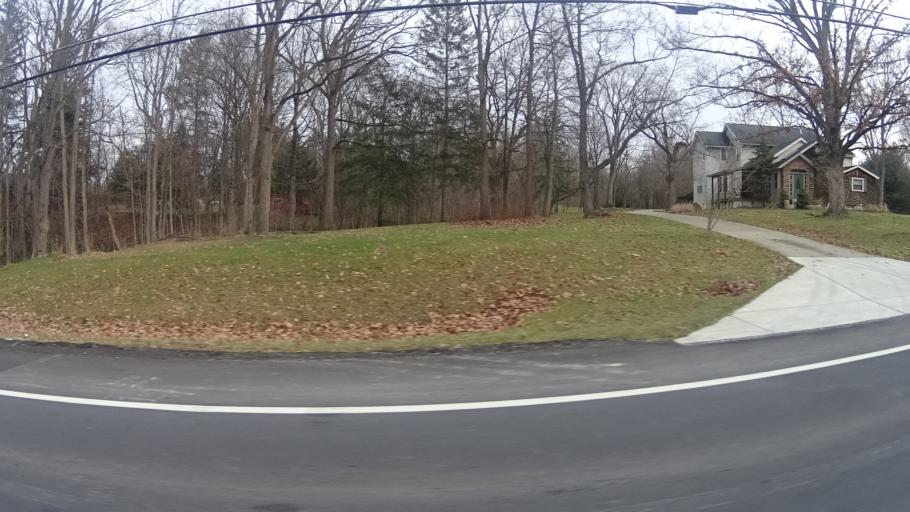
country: US
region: Ohio
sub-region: Cuyahoga County
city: Olmsted Falls
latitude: 41.3066
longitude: -81.9135
